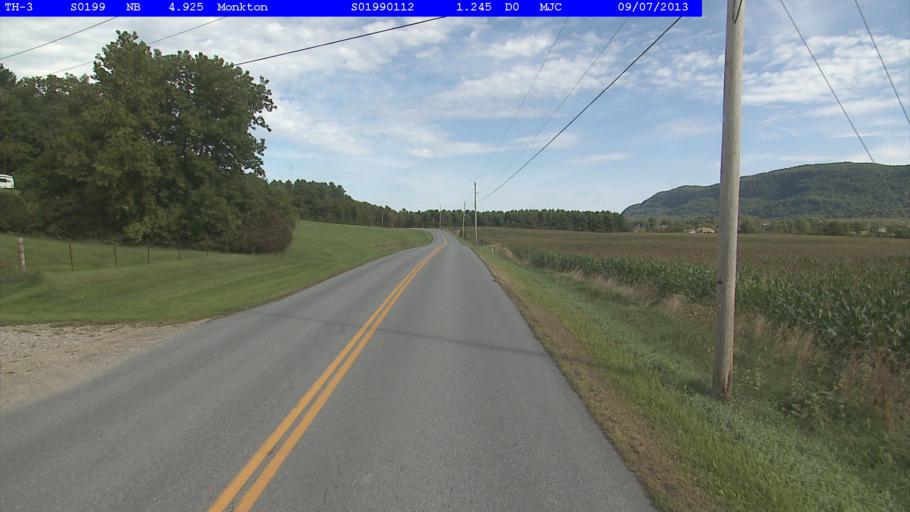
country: US
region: Vermont
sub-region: Addison County
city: Bristol
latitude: 44.1985
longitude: -73.1101
